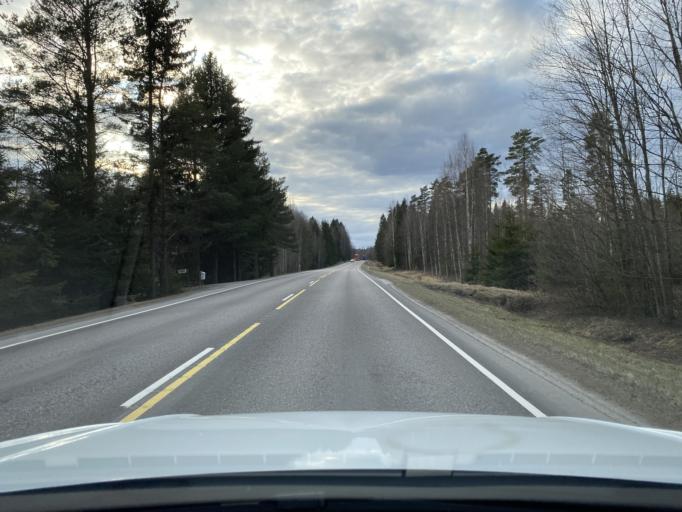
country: FI
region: Haeme
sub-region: Haemeenlinna
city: Renko
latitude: 60.7919
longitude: 24.1160
